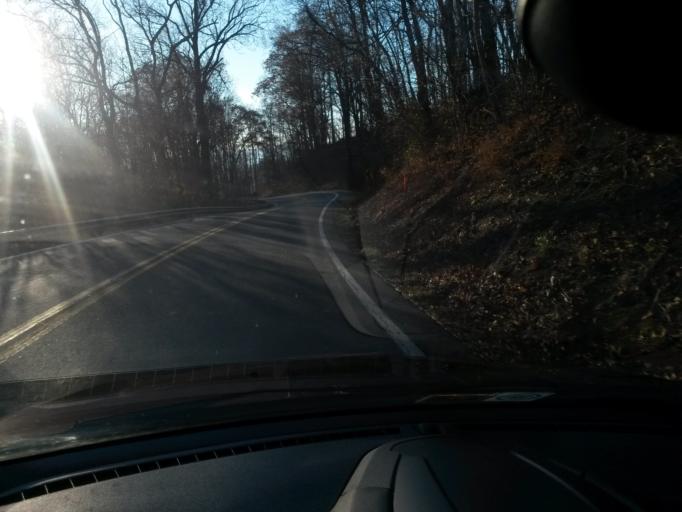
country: US
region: Virginia
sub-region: City of Buena Vista
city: Buena Vista
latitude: 37.7154
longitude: -79.2469
